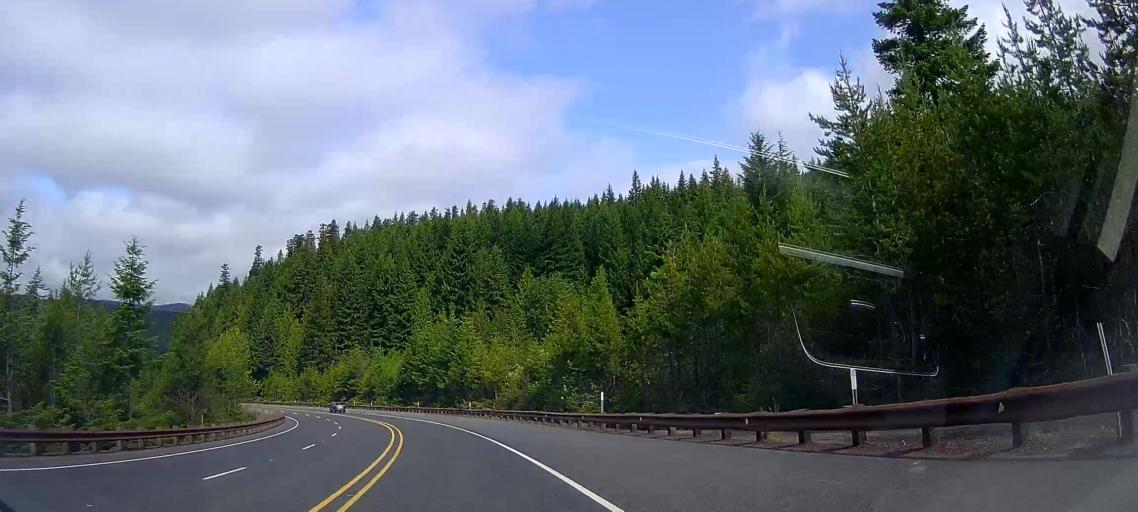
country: US
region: Oregon
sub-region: Clackamas County
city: Mount Hood Village
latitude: 45.2407
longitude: -121.7004
